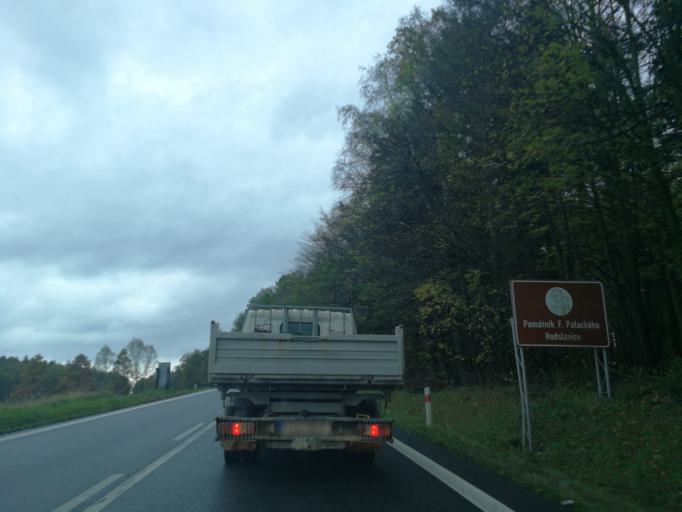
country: CZ
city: Hodslavice
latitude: 49.5138
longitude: 18.0094
